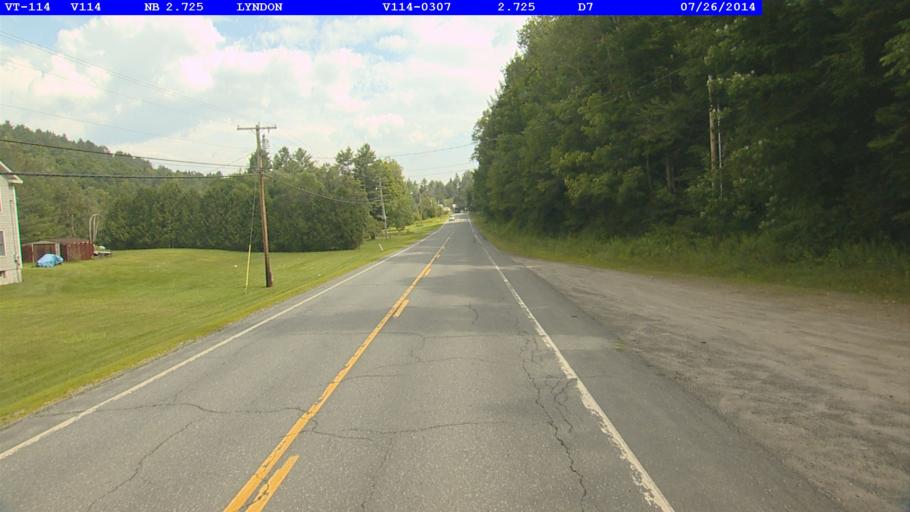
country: US
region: Vermont
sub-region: Caledonia County
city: Lyndonville
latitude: 44.5654
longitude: -71.9571
